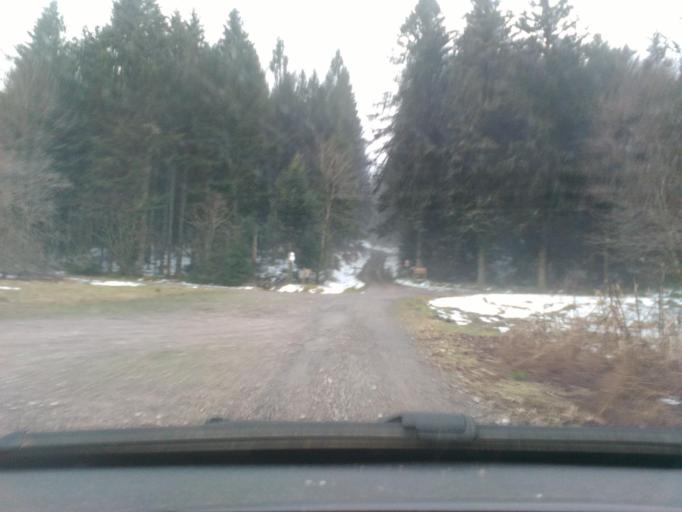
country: FR
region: Lorraine
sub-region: Departement des Vosges
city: Gerardmer
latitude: 48.1137
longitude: 6.8723
